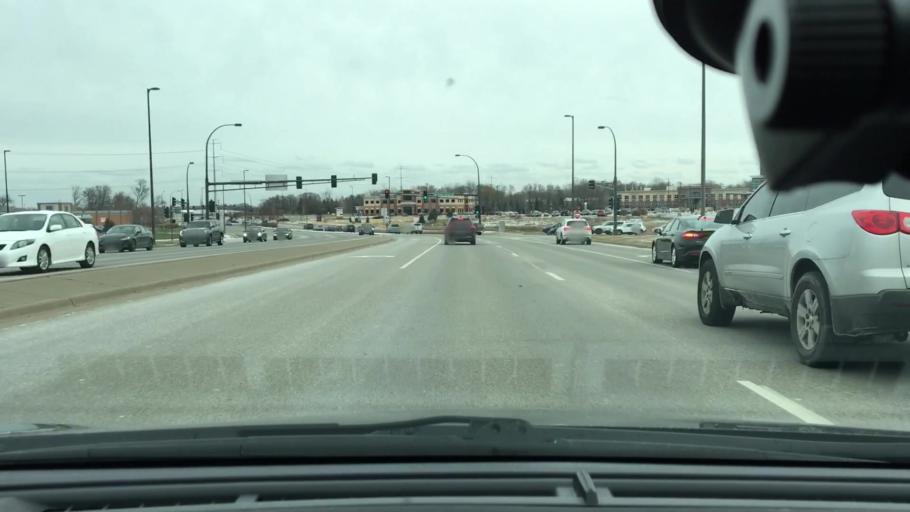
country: US
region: Minnesota
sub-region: Hennepin County
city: Maple Grove
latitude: 45.1282
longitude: -93.4843
